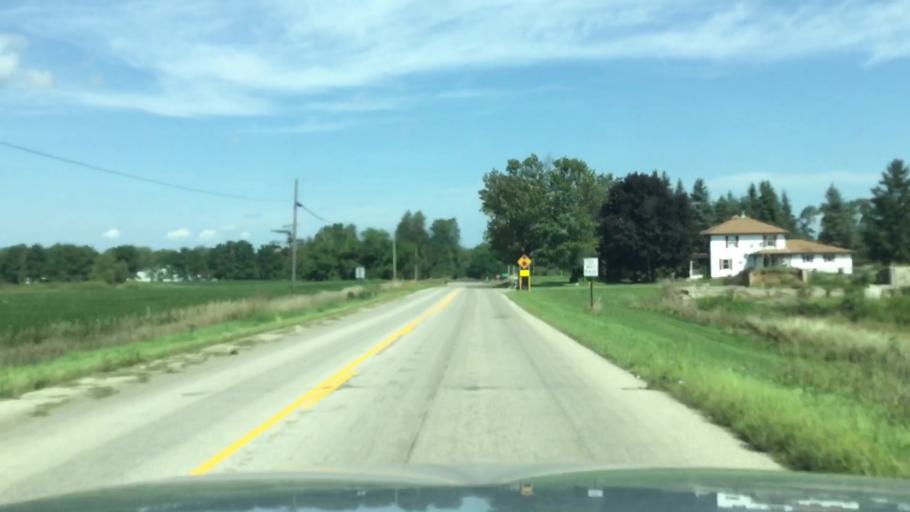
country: US
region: Michigan
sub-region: Jackson County
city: Brooklyn
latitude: 42.0460
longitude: -84.2765
